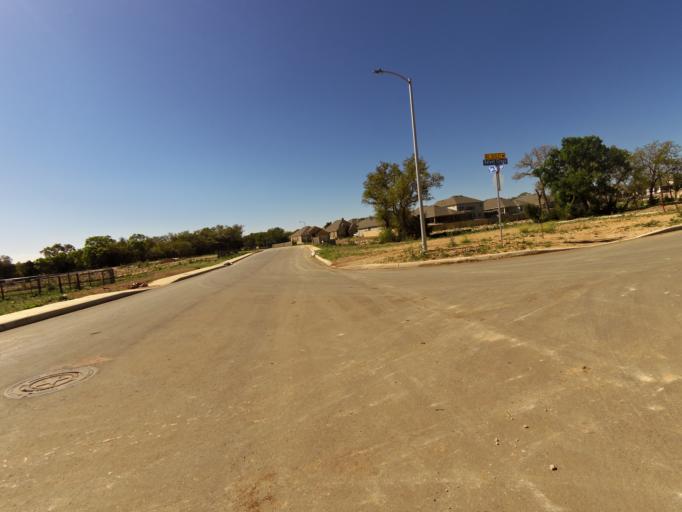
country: US
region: Texas
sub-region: Bexar County
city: Cross Mountain
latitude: 29.6828
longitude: -98.6442
